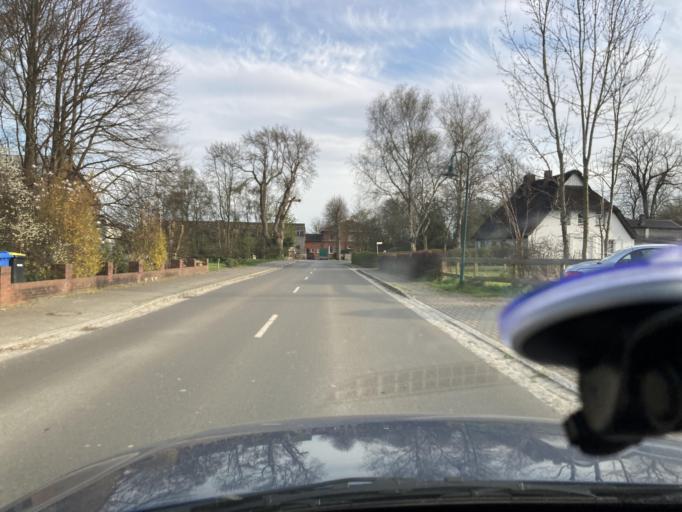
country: DE
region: Schleswig-Holstein
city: Schulp
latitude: 54.2443
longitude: 8.9372
